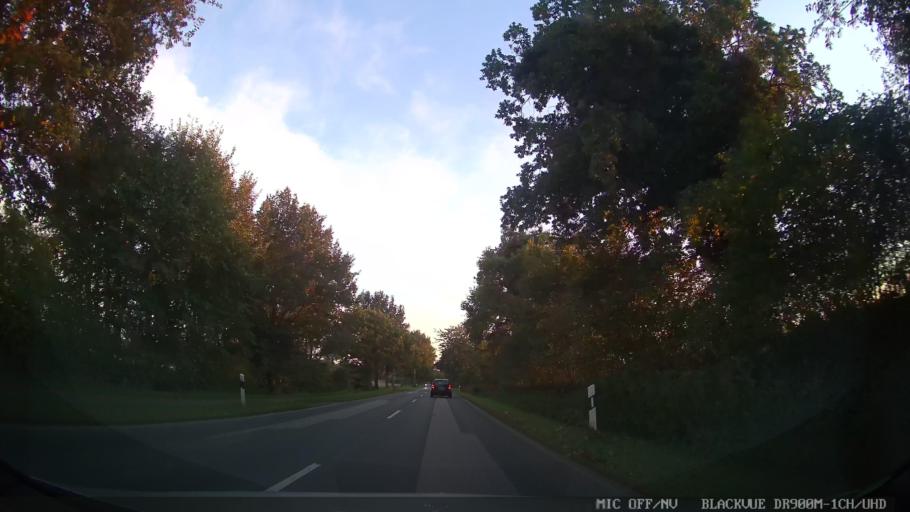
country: DE
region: Schleswig-Holstein
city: Susel
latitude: 54.0328
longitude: 10.6821
